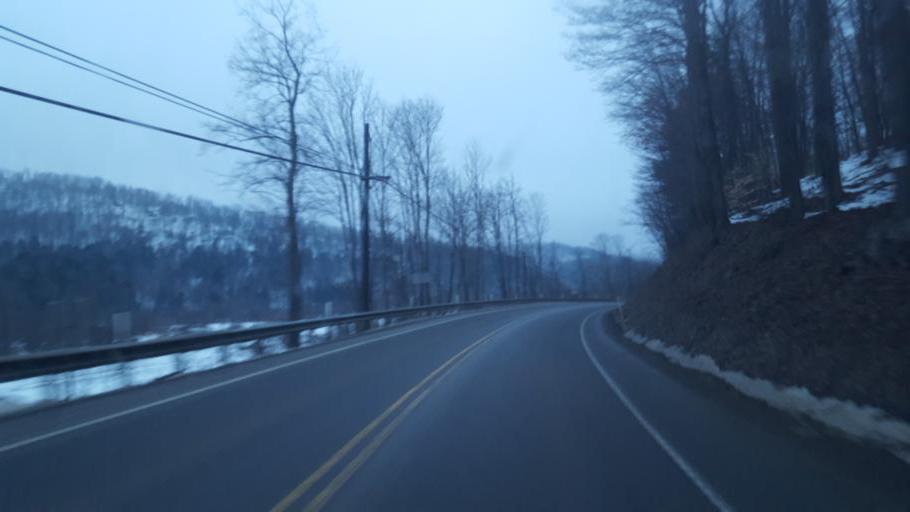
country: US
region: Pennsylvania
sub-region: Potter County
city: Coudersport
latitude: 41.7521
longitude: -78.0547
